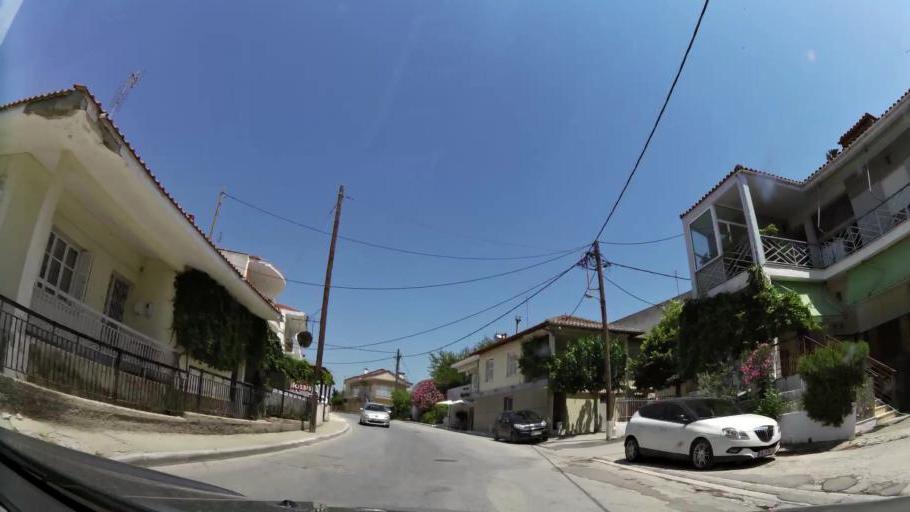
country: GR
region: Central Macedonia
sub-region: Nomos Thessalonikis
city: Epanomi
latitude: 40.4297
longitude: 22.9275
